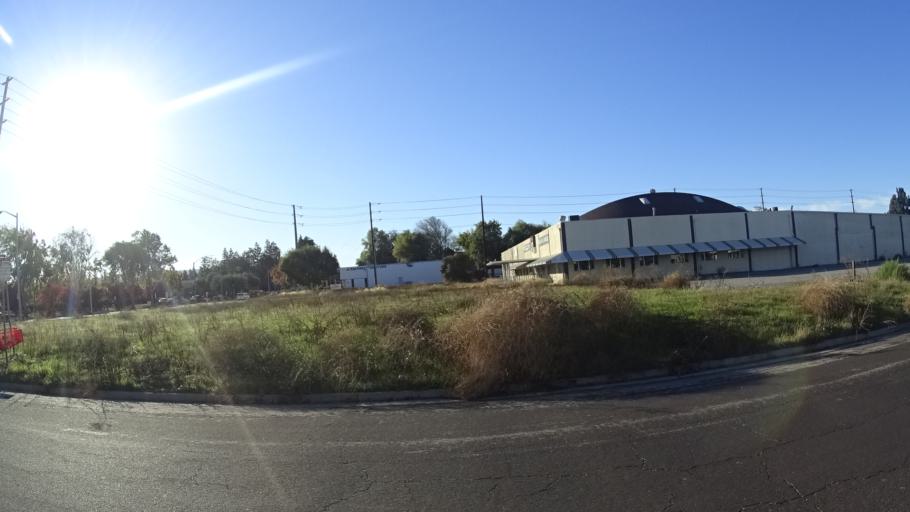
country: US
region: California
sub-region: Santa Clara County
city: Santa Clara
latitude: 37.3744
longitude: -121.9926
